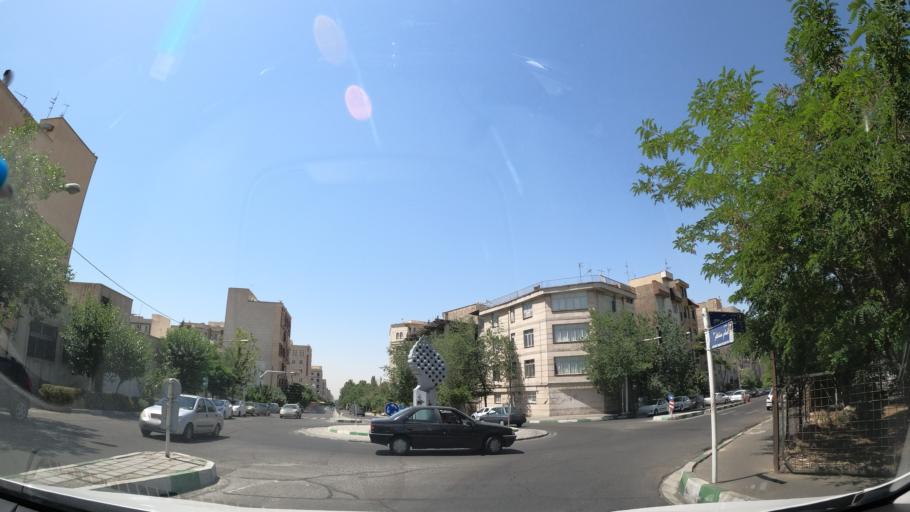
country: IR
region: Tehran
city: Tehran
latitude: 35.7260
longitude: 51.3694
